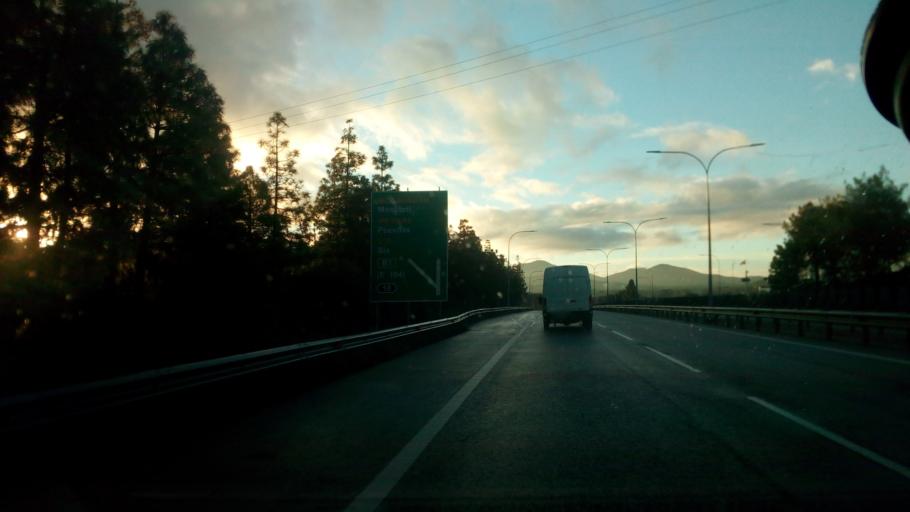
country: CY
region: Larnaka
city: Mosfiloti
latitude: 34.9515
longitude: 33.4092
